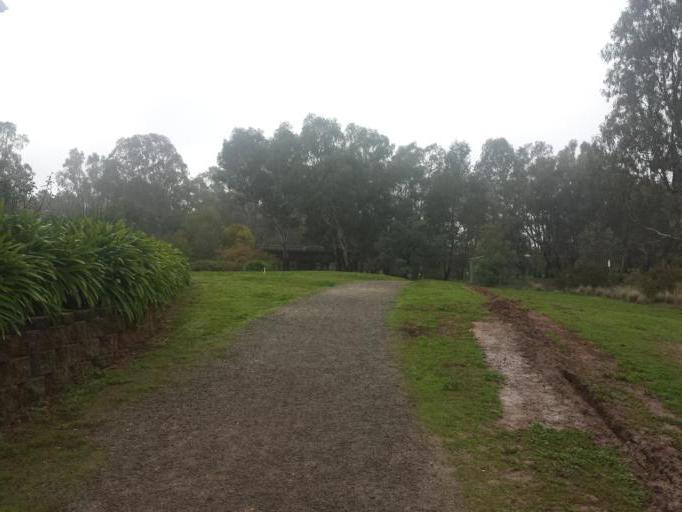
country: AU
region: Victoria
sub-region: Benalla
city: Benalla
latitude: -36.5484
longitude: 145.9754
